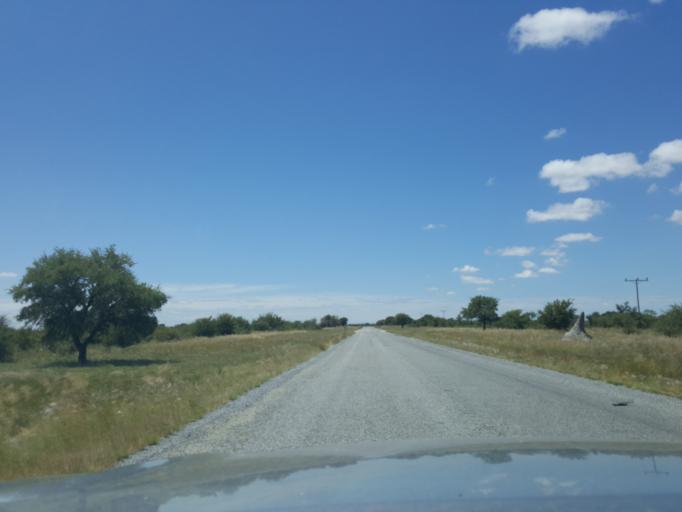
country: BW
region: Central
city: Nata
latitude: -20.1559
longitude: 25.8302
